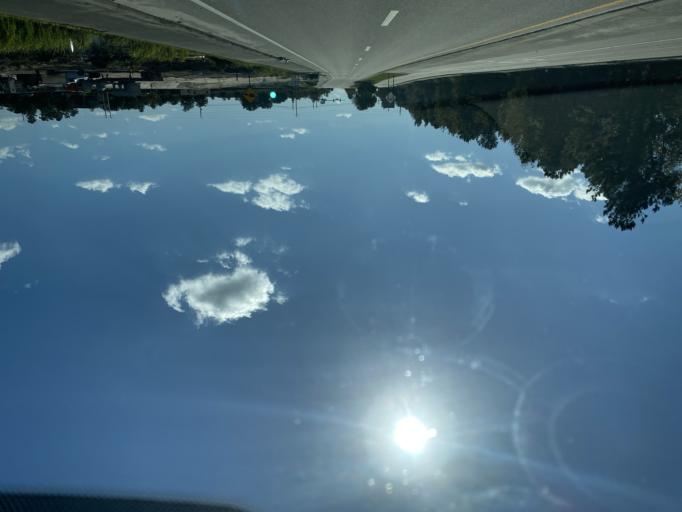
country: US
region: Florida
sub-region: Seminole County
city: Heathrow
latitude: 28.8107
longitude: -81.3479
